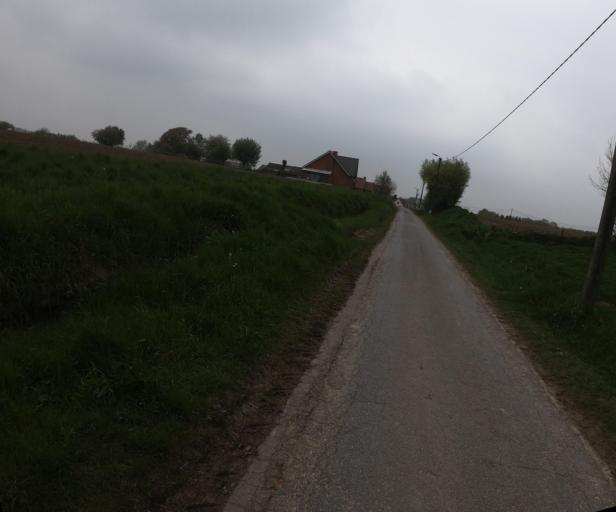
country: BE
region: Flanders
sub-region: Provincie Vlaams-Brabant
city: Pepingen
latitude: 50.7385
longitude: 4.1538
